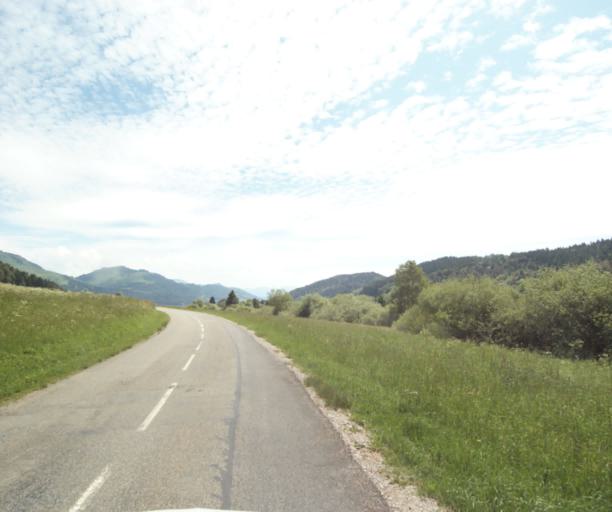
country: FR
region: Rhone-Alpes
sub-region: Departement de la Haute-Savoie
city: Perrignier
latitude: 46.2744
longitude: 6.4668
